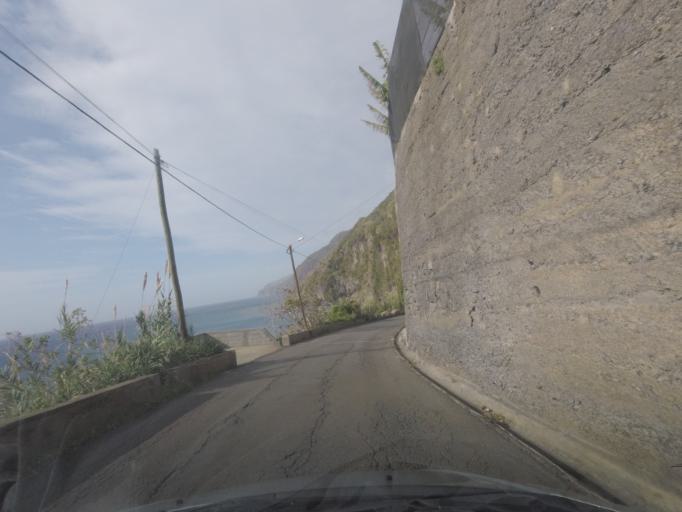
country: PT
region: Madeira
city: Ponta do Sol
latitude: 32.6890
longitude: -17.1188
